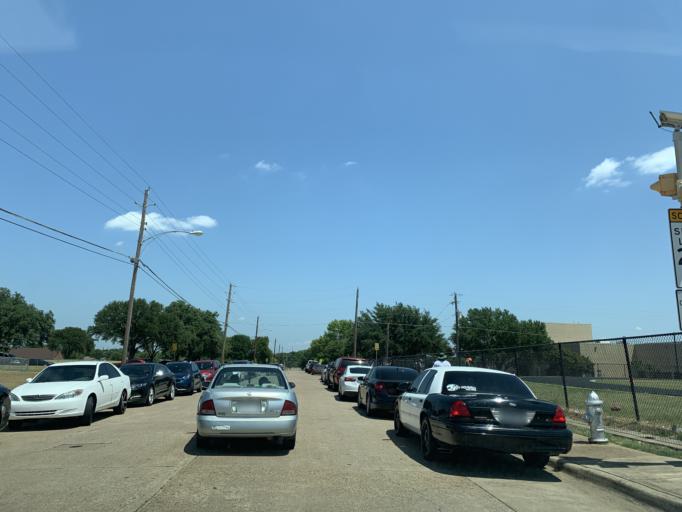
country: US
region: Texas
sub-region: Dallas County
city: Hutchins
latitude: 32.6927
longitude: -96.7675
